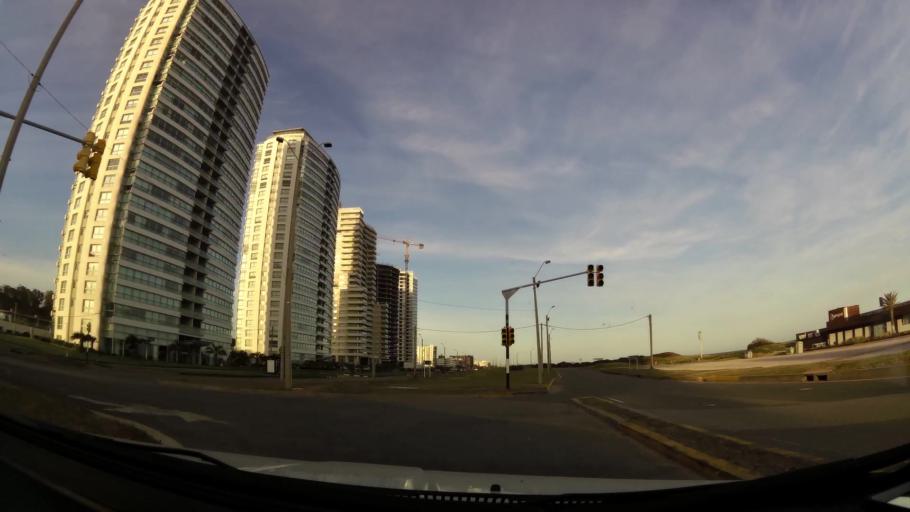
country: UY
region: Maldonado
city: Punta del Este
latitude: -34.9484
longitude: -54.9250
